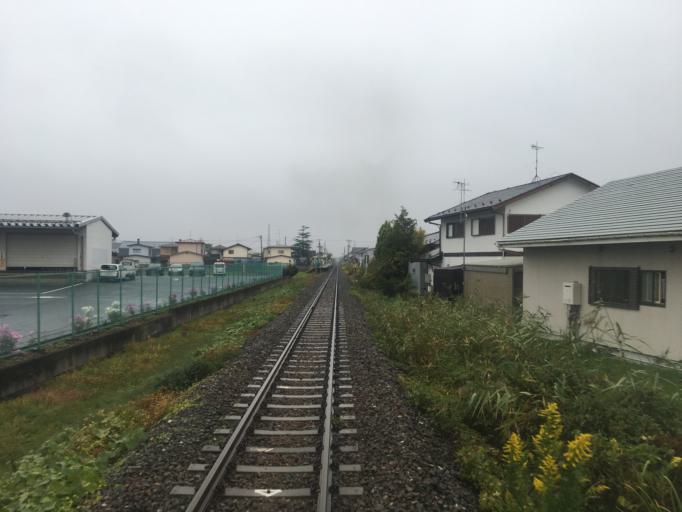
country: JP
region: Miyagi
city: Furukawa
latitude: 38.5726
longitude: 140.9350
